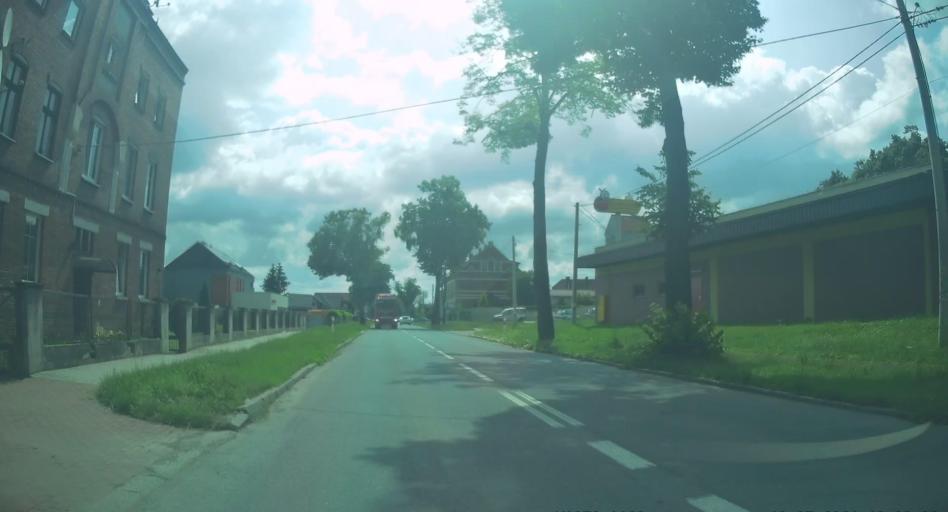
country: PL
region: Opole Voivodeship
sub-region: Powiat prudnicki
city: Glogowek
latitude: 50.3518
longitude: 17.8705
